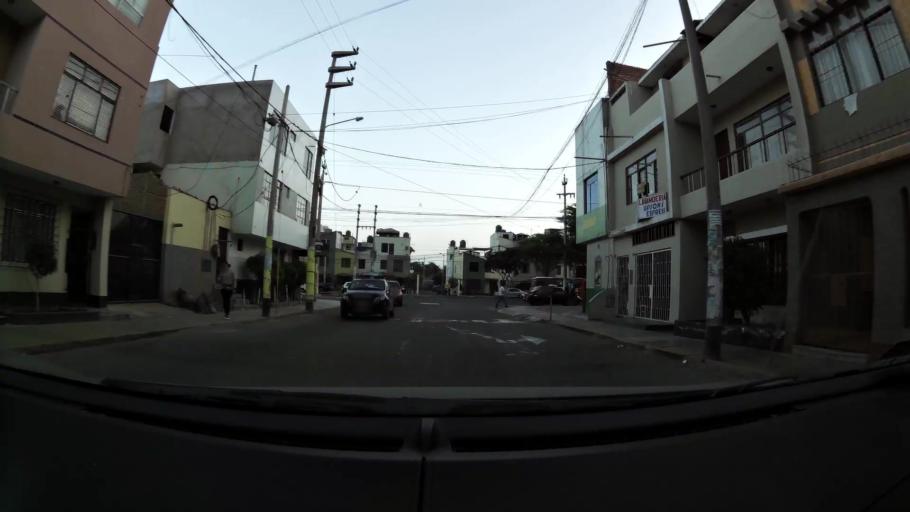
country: PE
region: La Libertad
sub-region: Provincia de Trujillo
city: Trujillo
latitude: -8.1018
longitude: -79.0410
